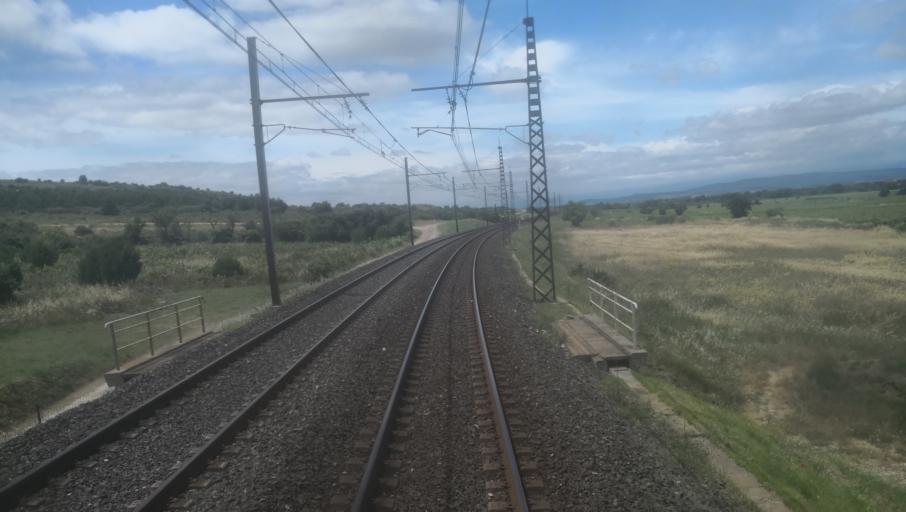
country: FR
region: Languedoc-Roussillon
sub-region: Departement de l'Aude
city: Nevian
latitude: 43.2103
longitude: 2.8974
